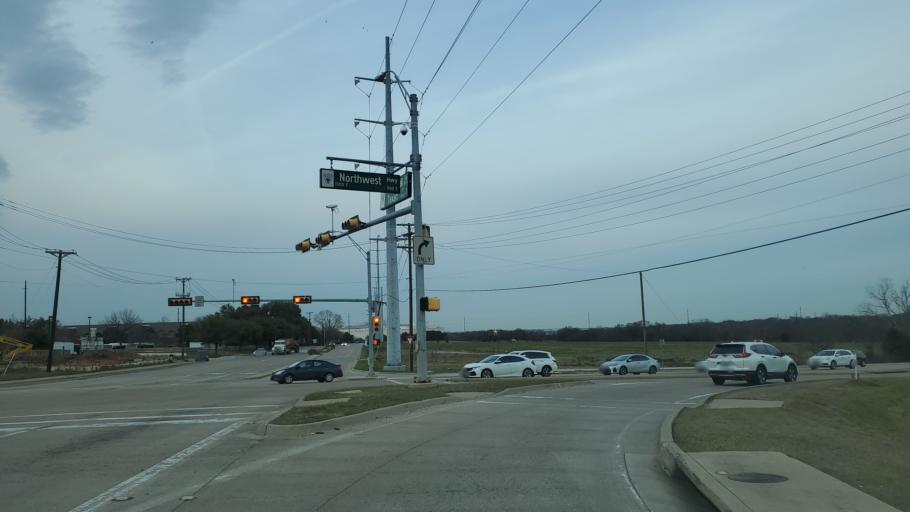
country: US
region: Texas
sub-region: Tarrant County
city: Grapevine
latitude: 32.9411
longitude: -97.0646
